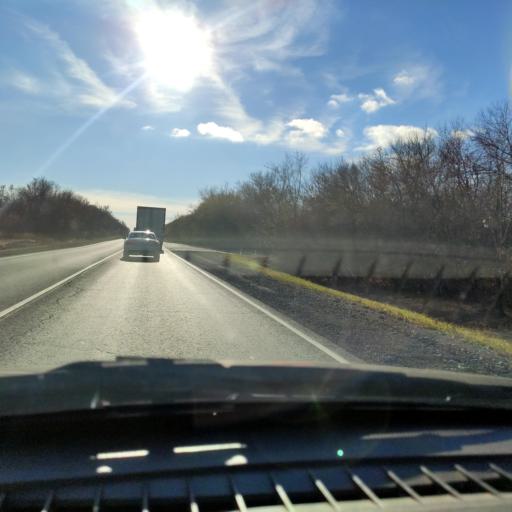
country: RU
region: Samara
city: Zhigulevsk
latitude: 53.3143
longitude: 49.3609
